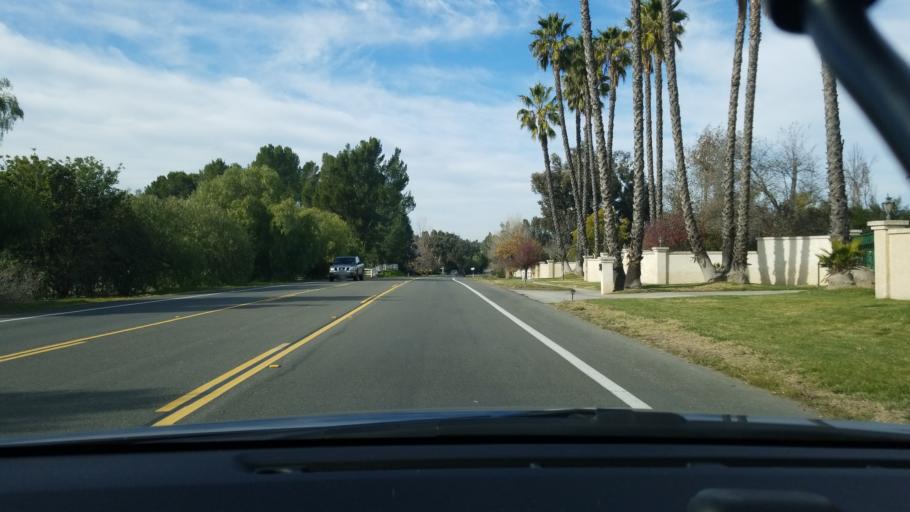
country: US
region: California
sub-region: Riverside County
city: Temecula
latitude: 33.4831
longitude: -117.1343
